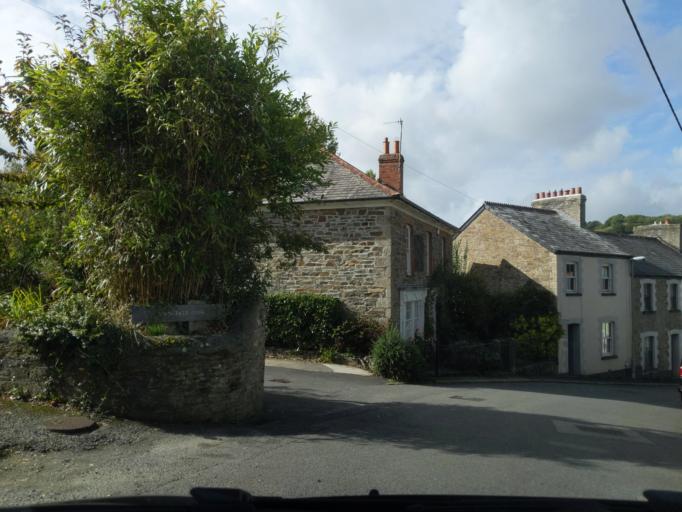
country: GB
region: England
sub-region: Cornwall
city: Lostwithiel
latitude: 50.4070
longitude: -4.6638
